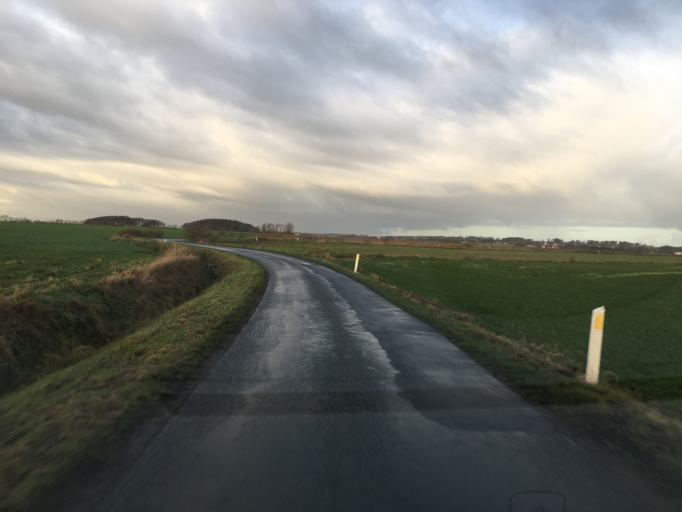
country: DK
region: South Denmark
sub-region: Tonder Kommune
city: Sherrebek
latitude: 55.1419
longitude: 8.8261
